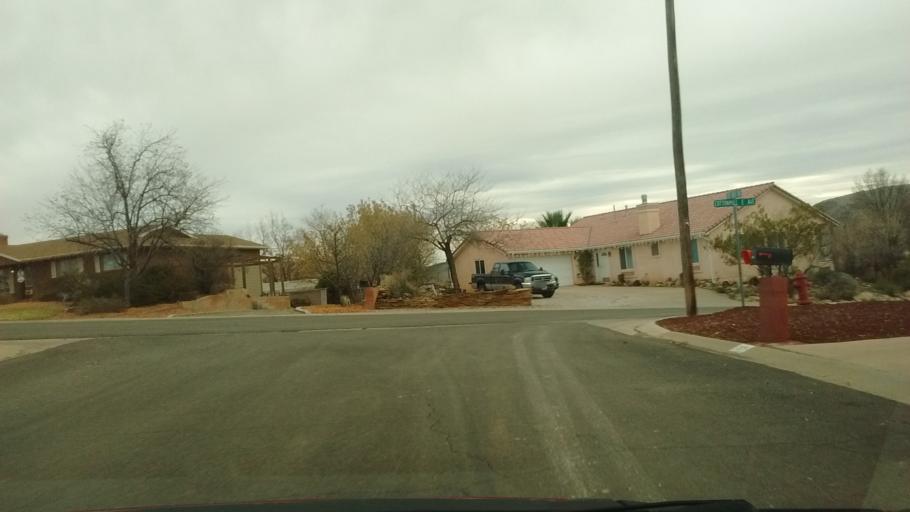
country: US
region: Utah
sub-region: Washington County
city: Washington
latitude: 37.1343
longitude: -113.4977
